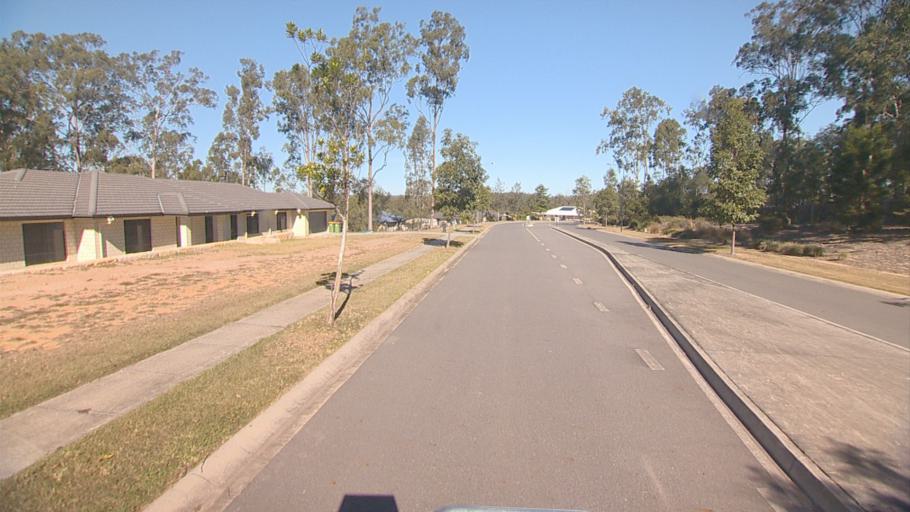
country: AU
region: Queensland
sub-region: Logan
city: North Maclean
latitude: -27.8237
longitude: 152.9802
